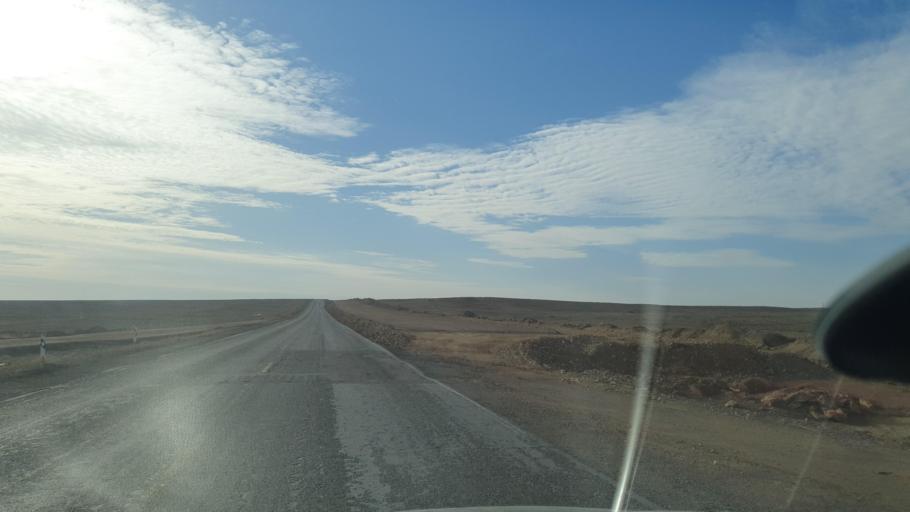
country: KZ
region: Qaraghandy
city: Saryshaghan
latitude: 45.9935
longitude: 73.5721
